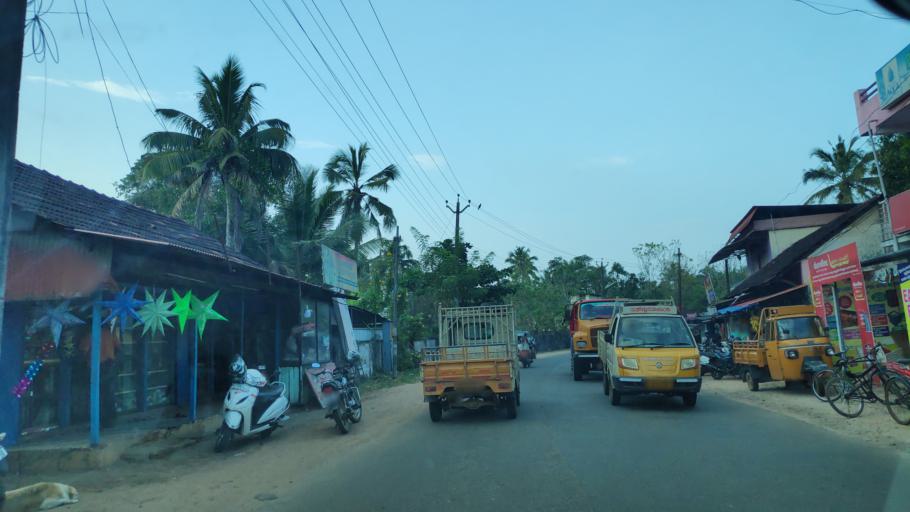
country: IN
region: Kerala
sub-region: Alappuzha
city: Shertallai
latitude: 9.6426
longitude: 76.3701
